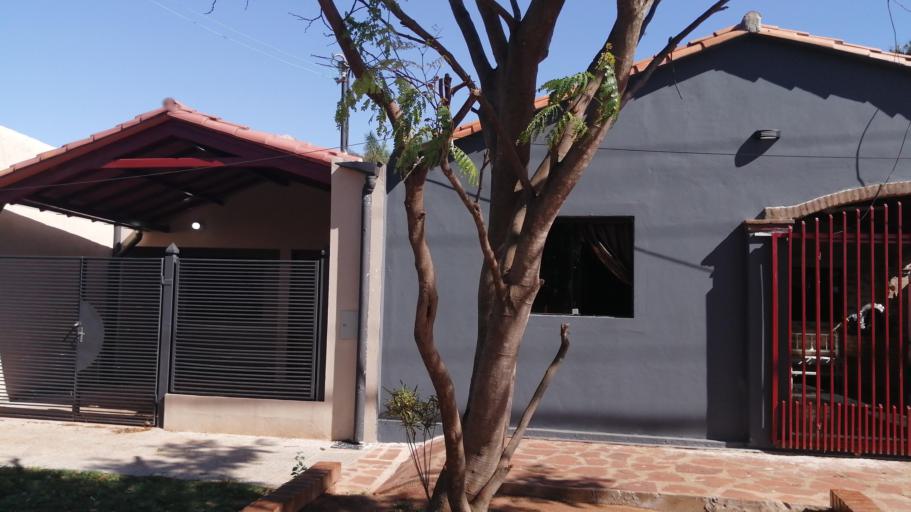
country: PY
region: Misiones
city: San Juan Bautista
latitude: -26.6757
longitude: -57.1432
